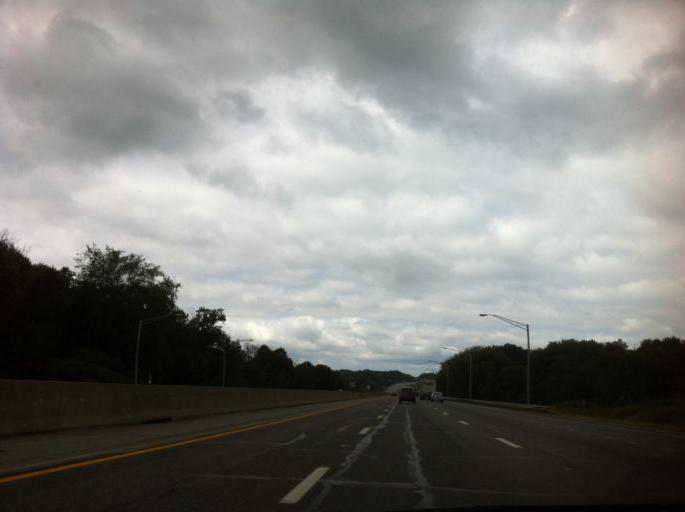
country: US
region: Ohio
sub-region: Portage County
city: Mantua
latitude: 41.2455
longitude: -81.2420
